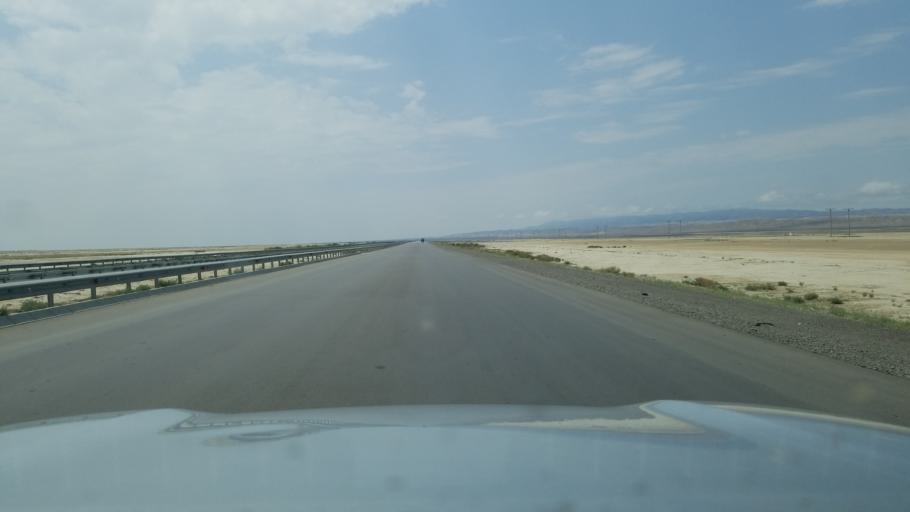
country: TM
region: Balkan
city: Gazanjyk
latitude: 39.2806
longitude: 55.2132
